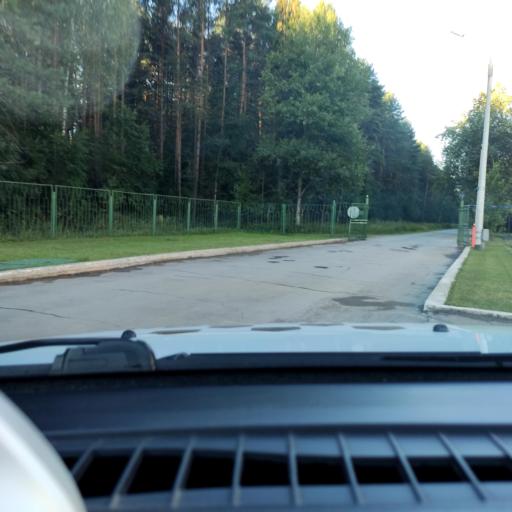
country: RU
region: Perm
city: Perm
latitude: 58.0573
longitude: 56.2407
